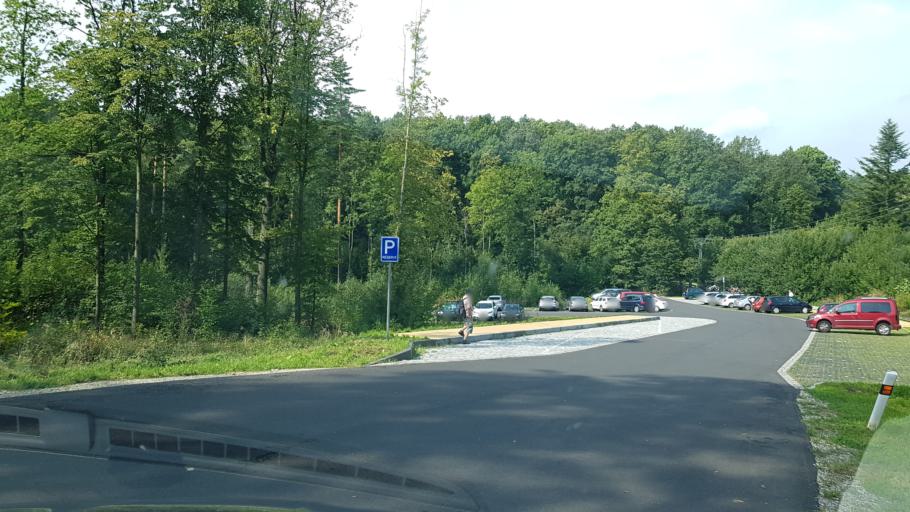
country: CZ
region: Olomoucky
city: Zlate Hory
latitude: 50.2555
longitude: 17.3678
